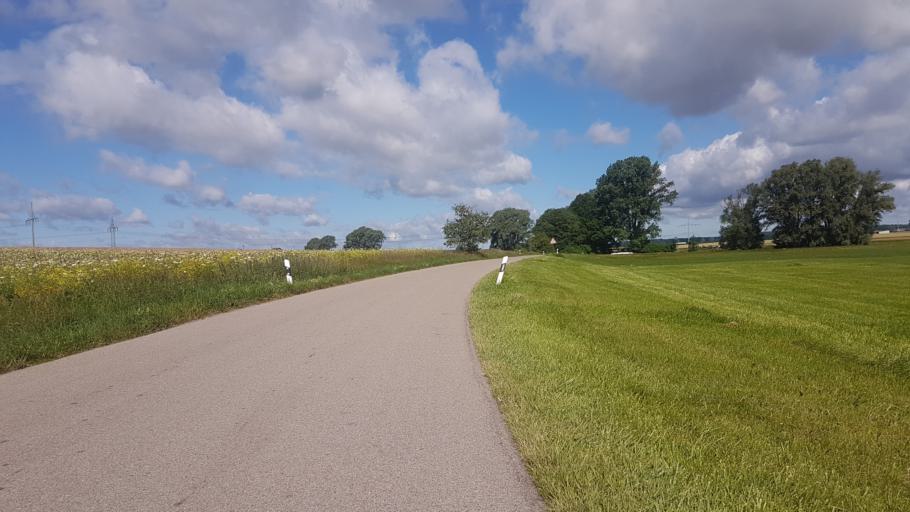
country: DE
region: Bavaria
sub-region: Regierungsbezirk Mittelfranken
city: Ornbau
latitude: 49.1788
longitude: 10.6454
